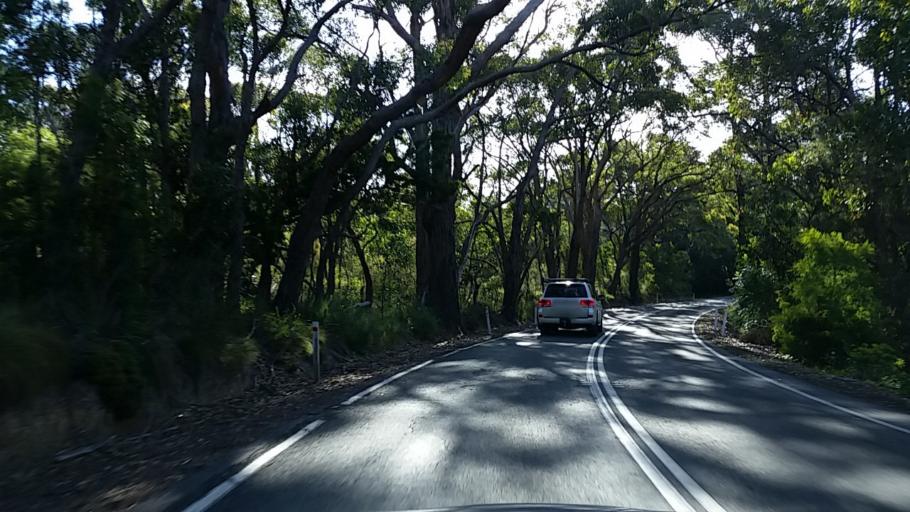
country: AU
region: South Australia
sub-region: Adelaide Hills
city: Stirling
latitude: -35.0269
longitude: 138.7625
